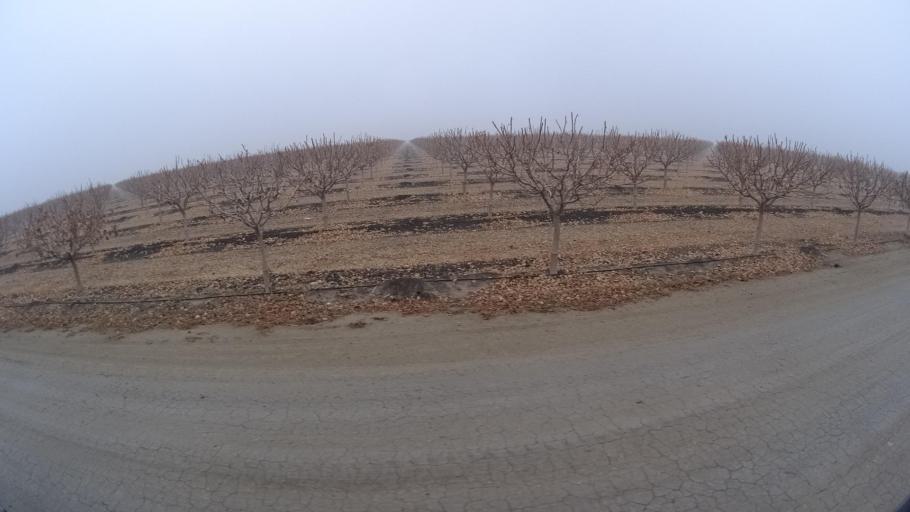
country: US
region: California
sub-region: Kern County
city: Buttonwillow
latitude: 35.4572
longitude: -119.5650
